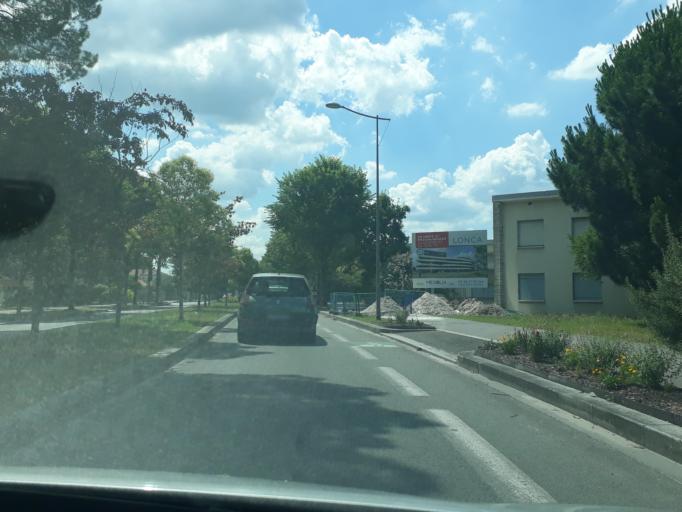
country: FR
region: Aquitaine
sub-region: Departement de la Gironde
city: Merignac
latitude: 44.8421
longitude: -0.6614
